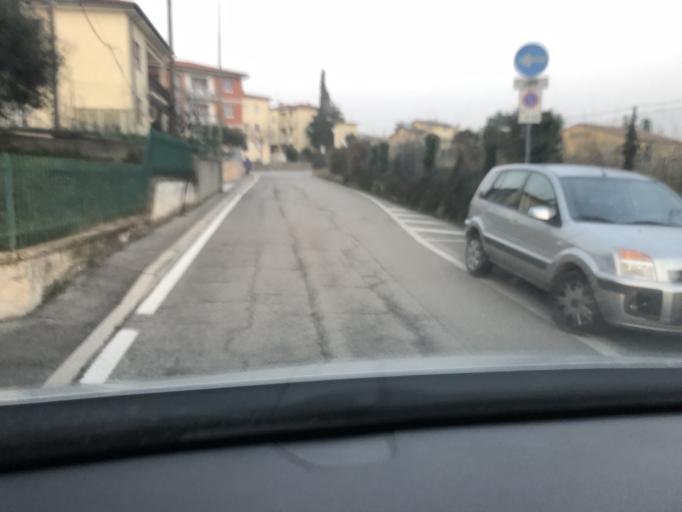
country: IT
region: Veneto
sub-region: Provincia di Verona
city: Sommacampagna
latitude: 45.4052
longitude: 10.8377
